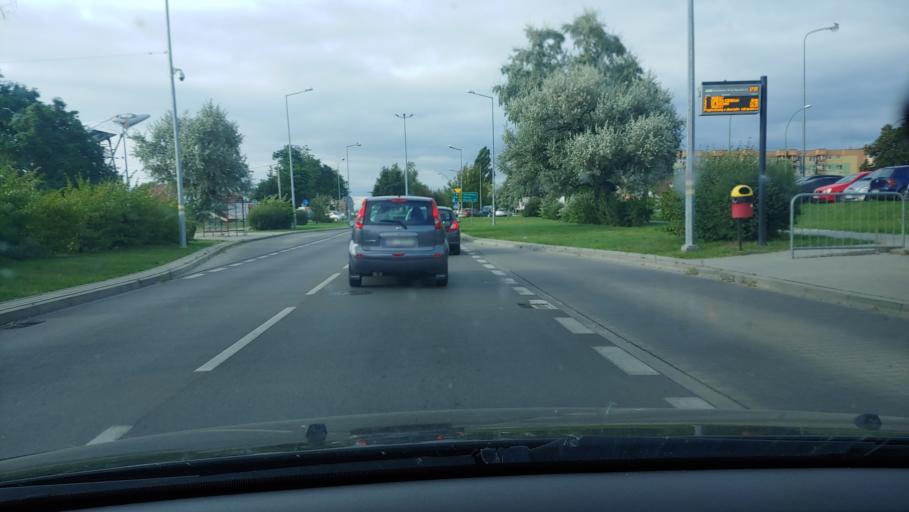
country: PL
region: Subcarpathian Voivodeship
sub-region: Powiat mielecki
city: Mielec
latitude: 50.2898
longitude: 21.4619
